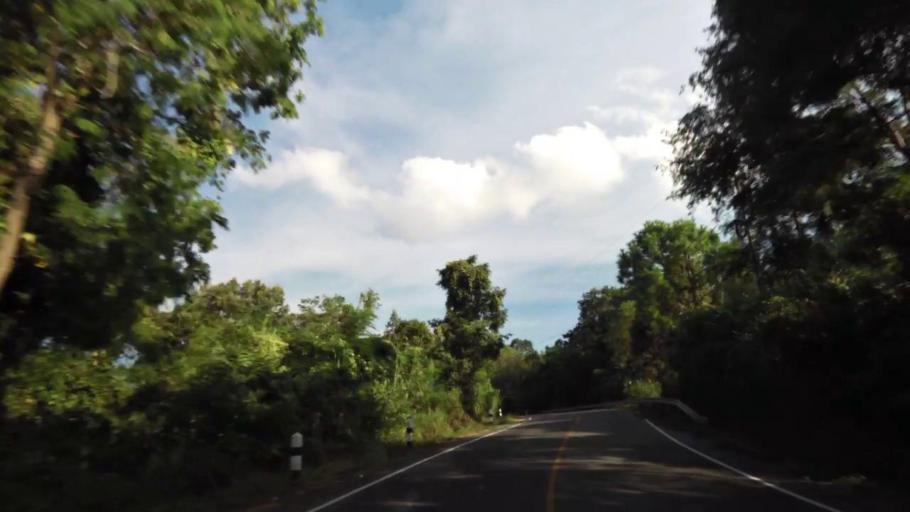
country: TH
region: Chiang Rai
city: Khun Tan
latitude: 19.8765
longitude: 100.3167
